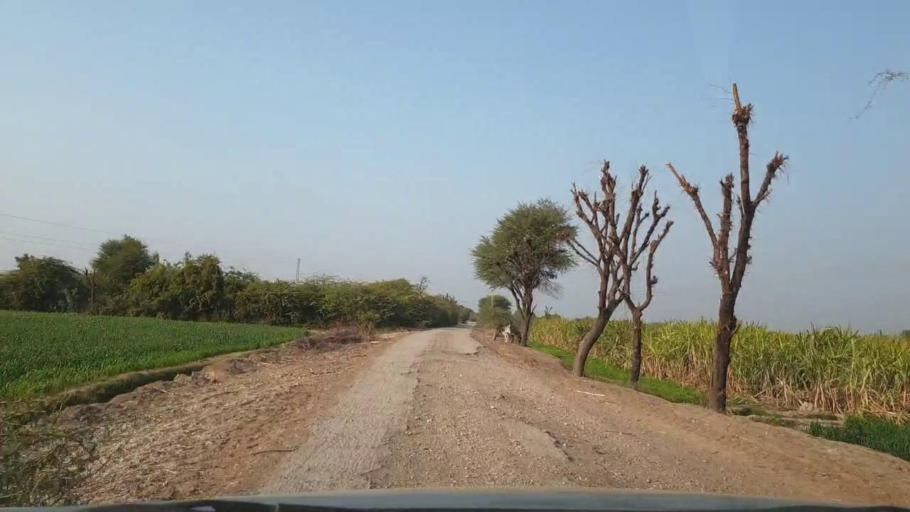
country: PK
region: Sindh
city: Tando Adam
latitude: 25.6851
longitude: 68.6328
